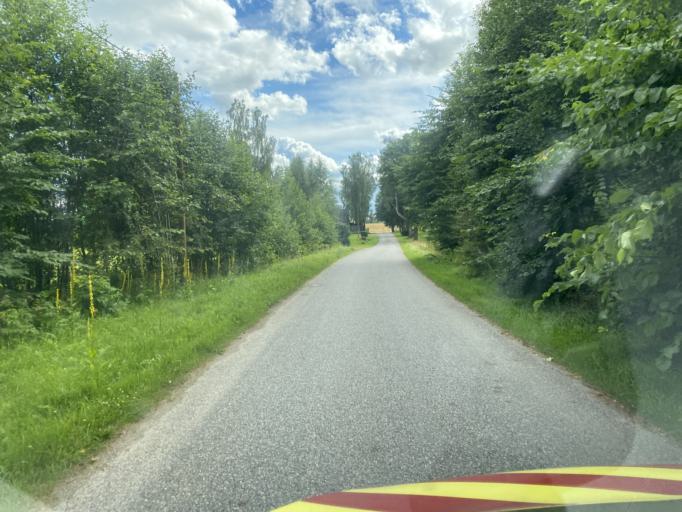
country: EE
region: Viljandimaa
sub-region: Viiratsi vald
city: Viiratsi
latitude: 58.3943
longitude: 25.8218
